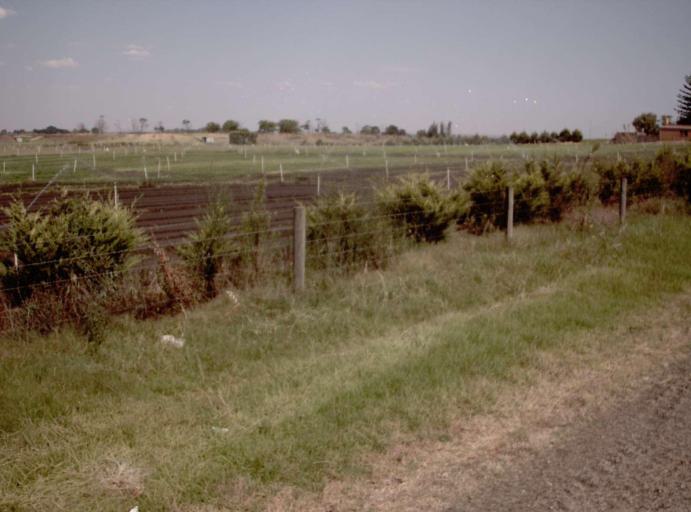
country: AU
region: Victoria
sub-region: Casey
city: Junction Village
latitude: -38.1479
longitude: 145.3213
